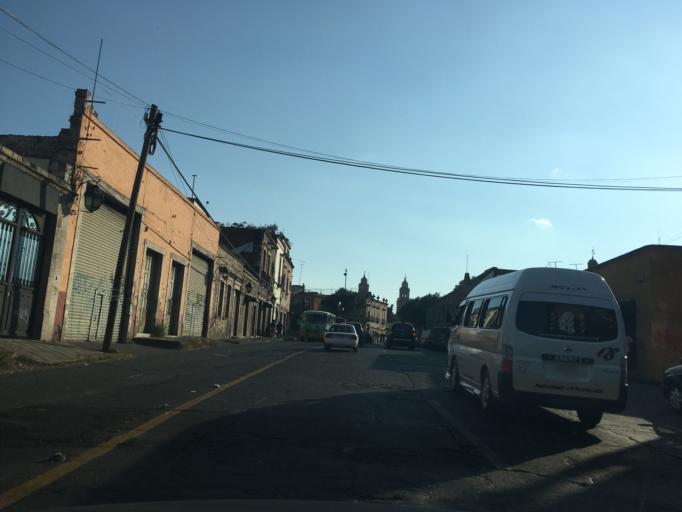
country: MX
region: Michoacan
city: Morelia
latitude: 19.7071
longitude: -101.1907
